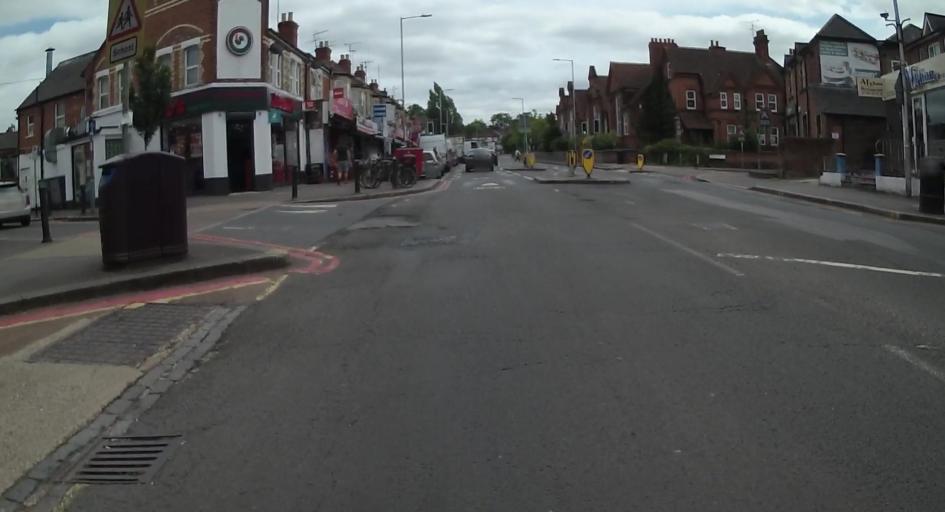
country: GB
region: England
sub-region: Wokingham
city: Earley
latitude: 51.4493
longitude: -0.9380
